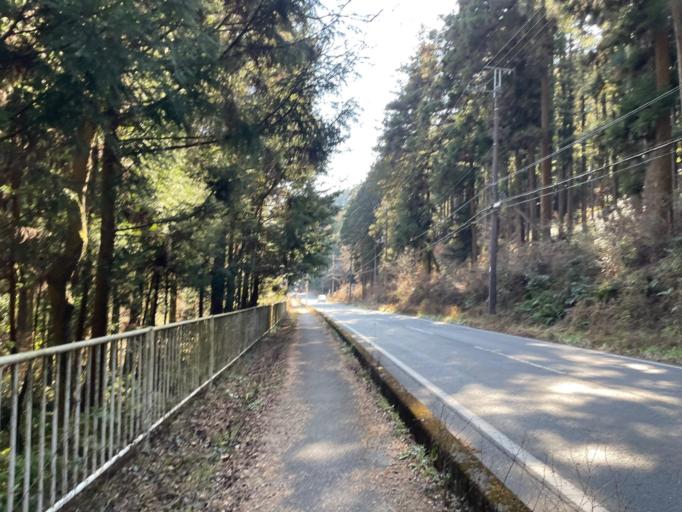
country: JP
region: Saitama
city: Hanno
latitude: 35.8545
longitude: 139.2481
